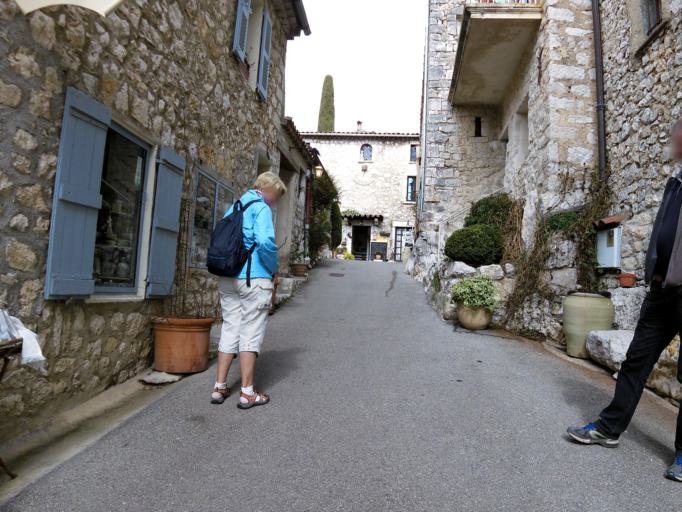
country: FR
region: Provence-Alpes-Cote d'Azur
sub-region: Departement des Alpes-Maritimes
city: Opio
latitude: 43.7196
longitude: 6.9786
